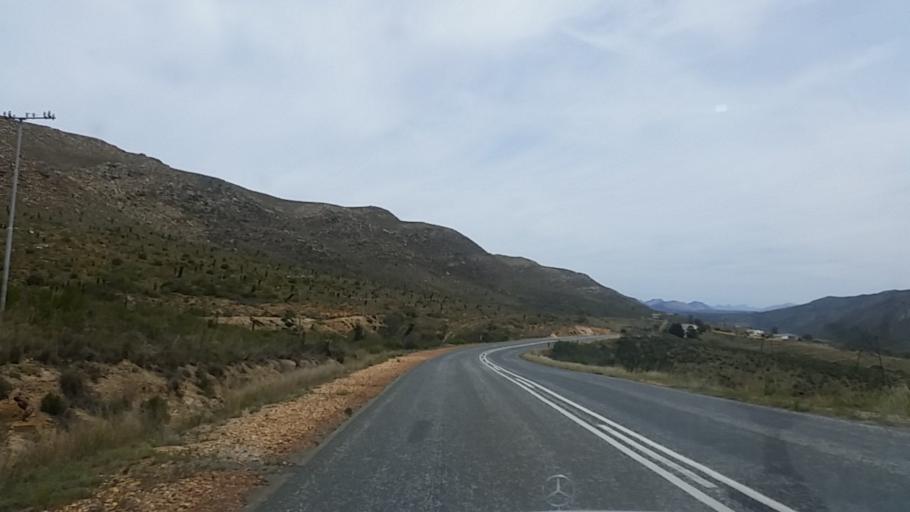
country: ZA
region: Western Cape
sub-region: Eden District Municipality
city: Knysna
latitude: -33.7425
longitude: 23.0009
